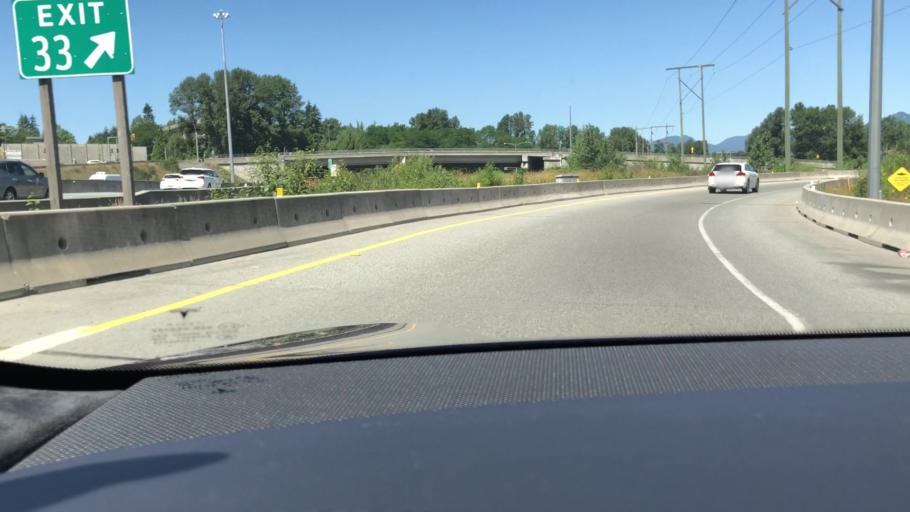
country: CA
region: British Columbia
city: Burnaby
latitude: 49.2426
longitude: -122.9643
